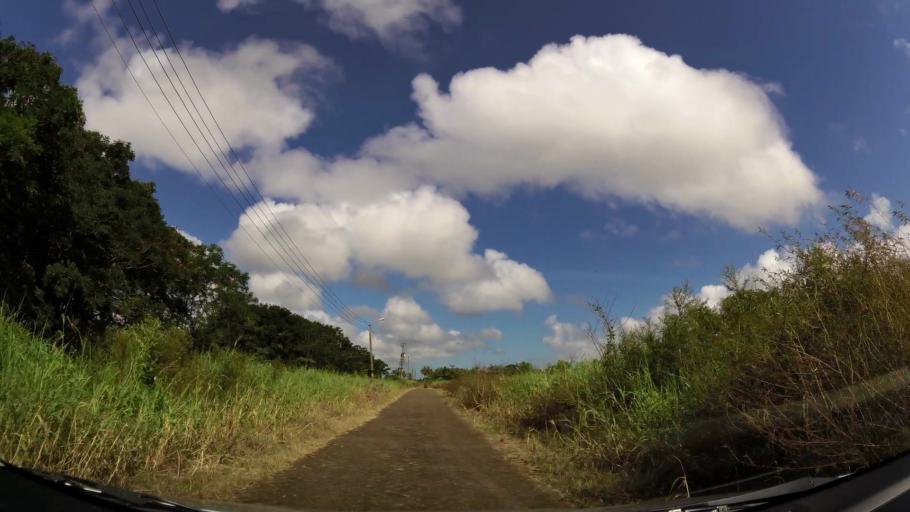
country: SR
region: Commewijne
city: Nieuw Amsterdam
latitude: 5.8779
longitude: -55.1122
